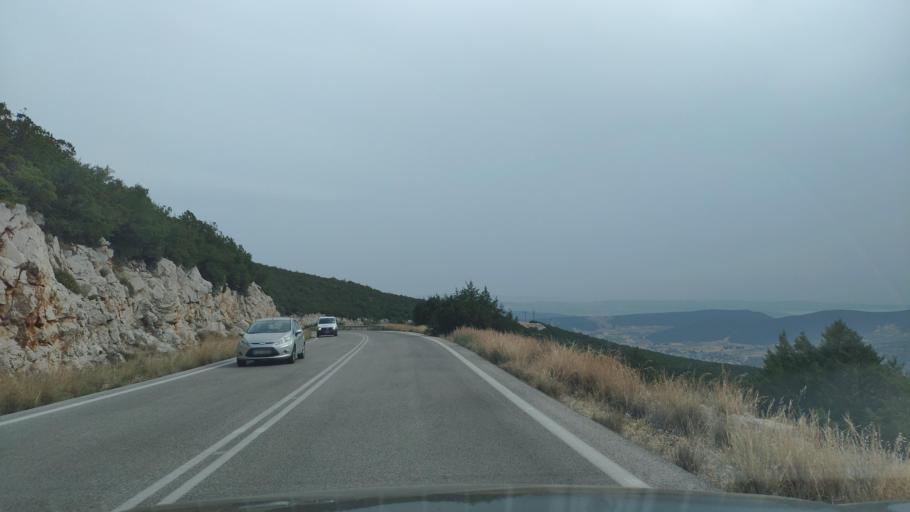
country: GR
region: Peloponnese
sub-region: Nomos Argolidos
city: Didyma
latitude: 37.4932
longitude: 23.1916
